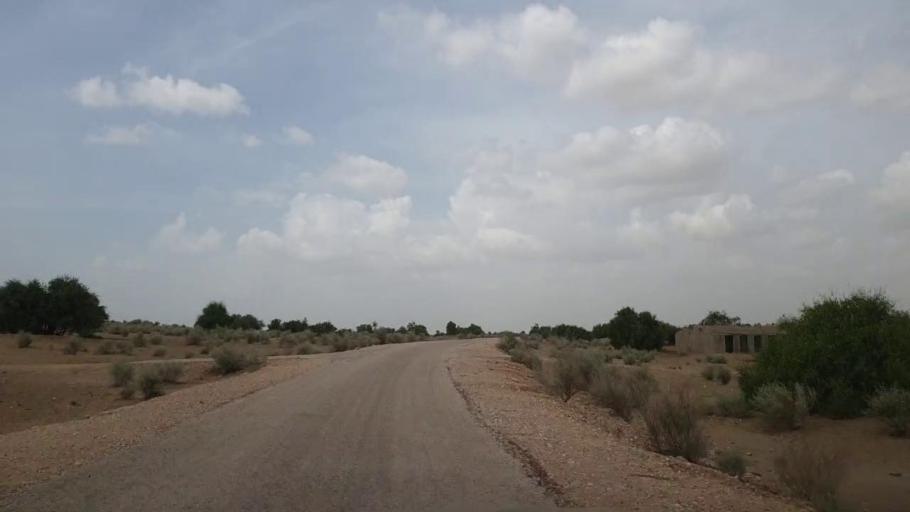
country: PK
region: Sindh
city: Kot Diji
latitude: 27.2145
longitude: 69.0831
